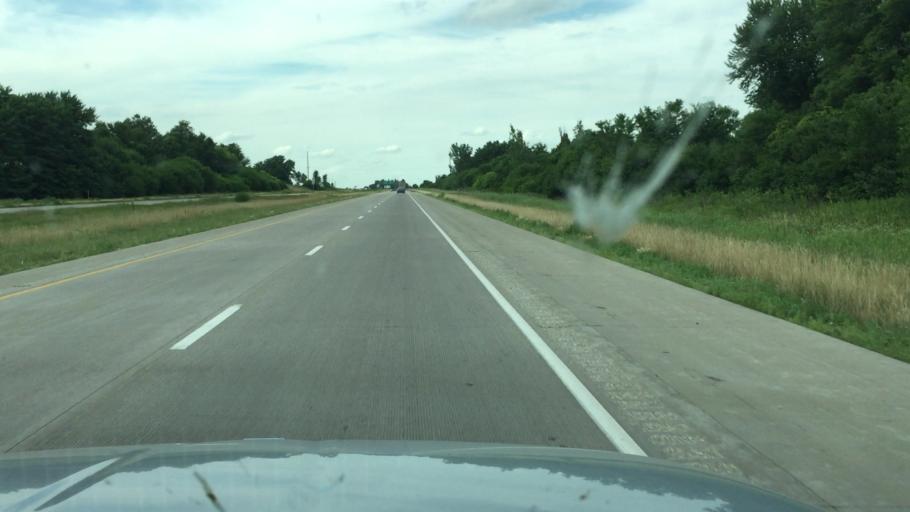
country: US
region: Iowa
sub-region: Scott County
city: Walcott
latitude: 41.5767
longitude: -90.6771
